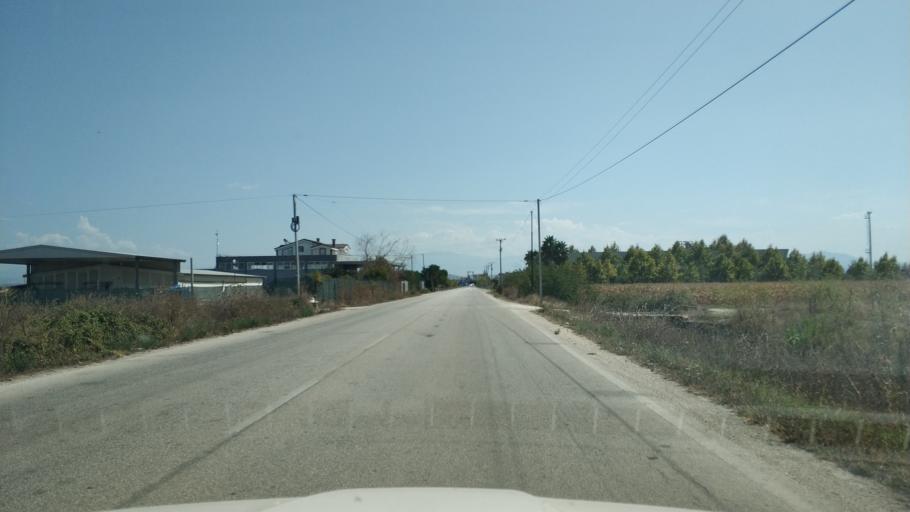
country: AL
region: Fier
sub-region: Rrethi i Lushnjes
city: Krutja e Poshtme
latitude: 40.8810
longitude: 19.6639
